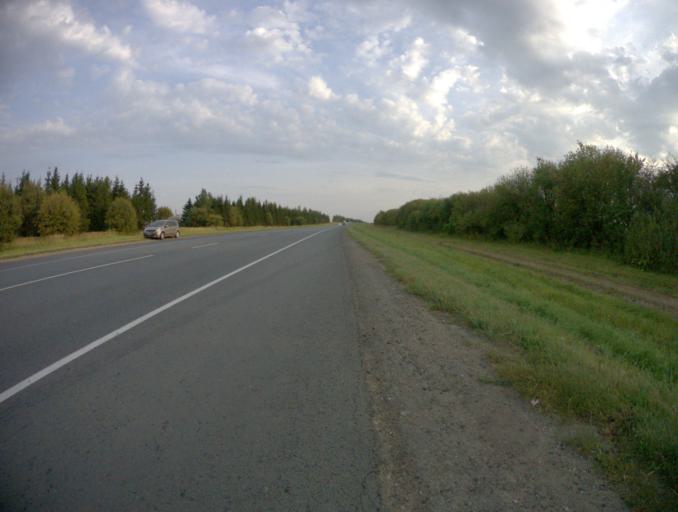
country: RU
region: Vladimir
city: Suzdal'
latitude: 56.3465
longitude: 40.4743
